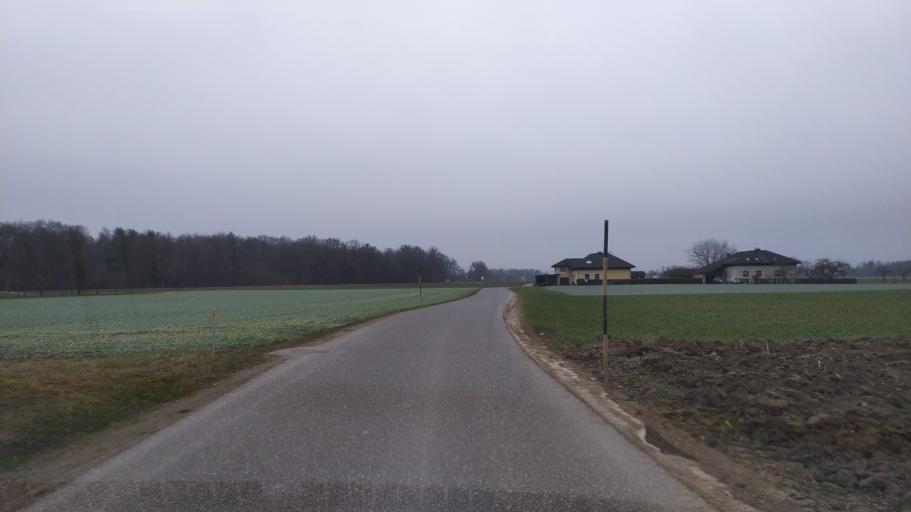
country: AT
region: Upper Austria
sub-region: Politischer Bezirk Perg
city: Perg
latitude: 48.2060
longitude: 14.7202
